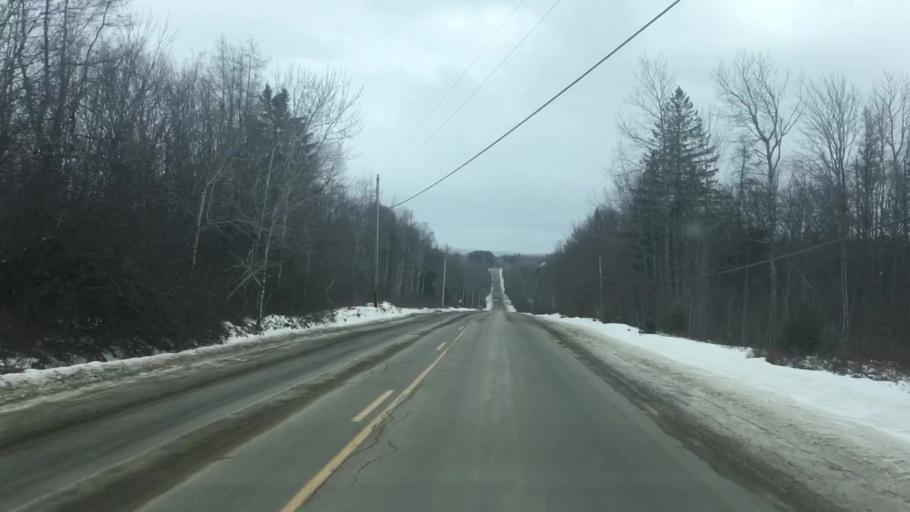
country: US
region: Maine
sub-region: Washington County
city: East Machias
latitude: 44.9716
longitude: -67.4484
